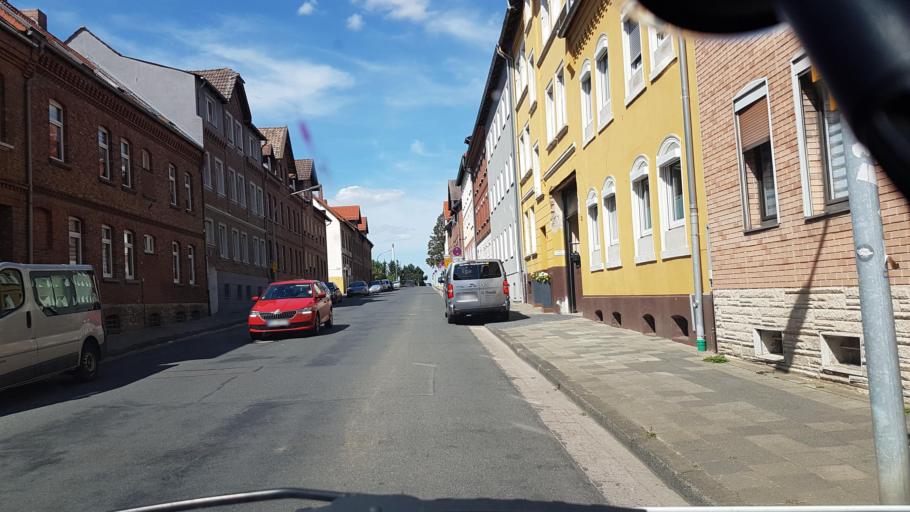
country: DE
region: Lower Saxony
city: Schoningen
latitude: 52.1411
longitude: 10.9745
